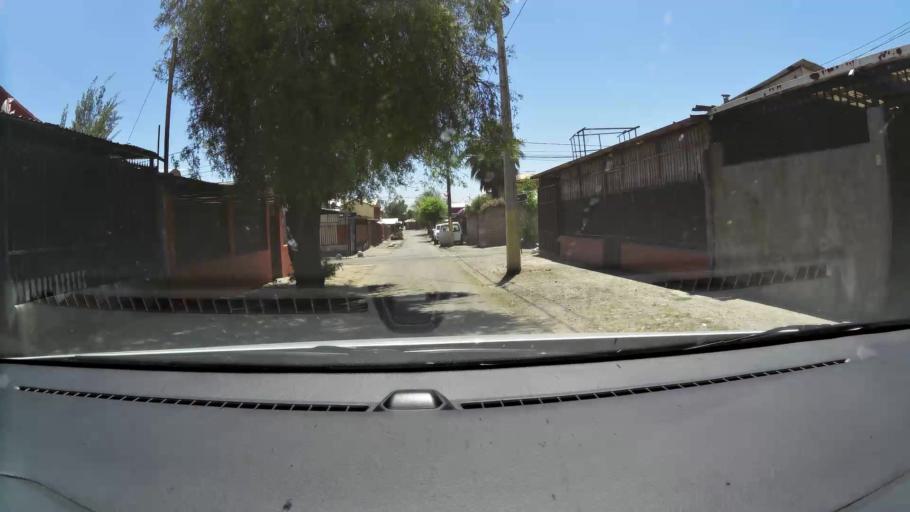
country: CL
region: Santiago Metropolitan
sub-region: Provincia de Maipo
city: San Bernardo
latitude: -33.5737
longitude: -70.6712
